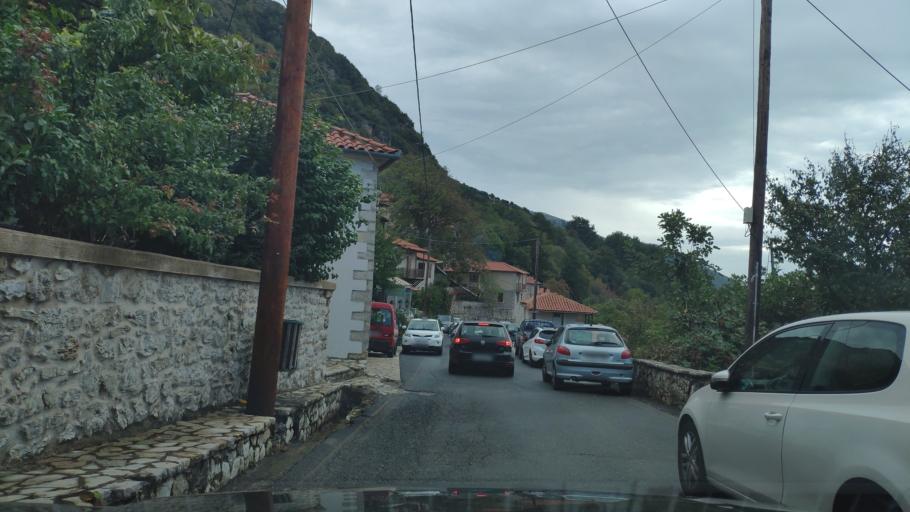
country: GR
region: Peloponnese
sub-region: Nomos Arkadias
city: Dimitsana
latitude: 37.5944
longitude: 22.0406
